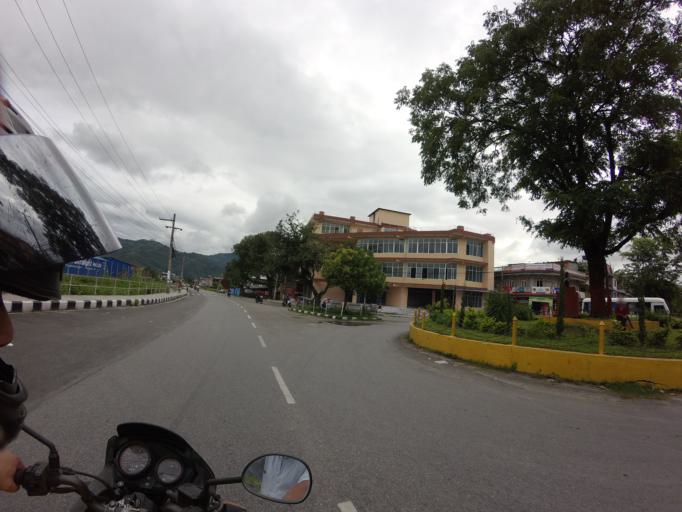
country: NP
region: Western Region
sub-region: Gandaki Zone
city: Pokhara
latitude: 28.1983
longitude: 83.9759
